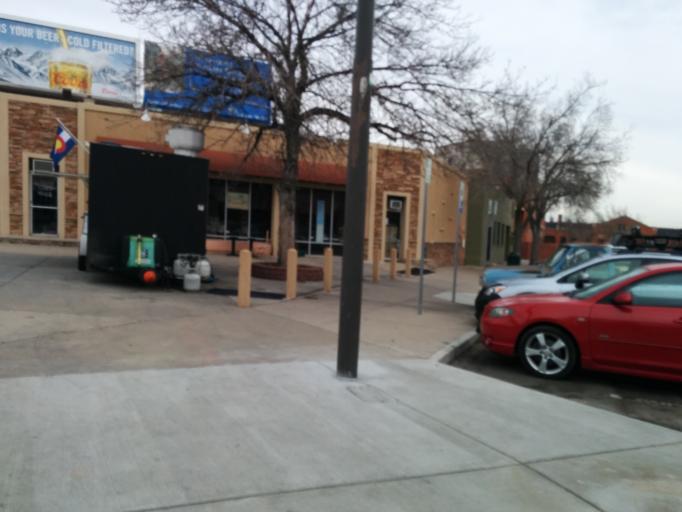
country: US
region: Colorado
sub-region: Larimer County
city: Fort Collins
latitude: 40.5891
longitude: -105.0767
